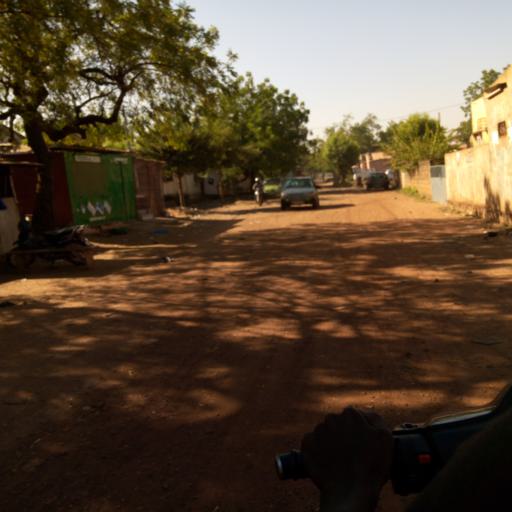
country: ML
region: Bamako
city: Bamako
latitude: 12.6563
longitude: -8.0193
